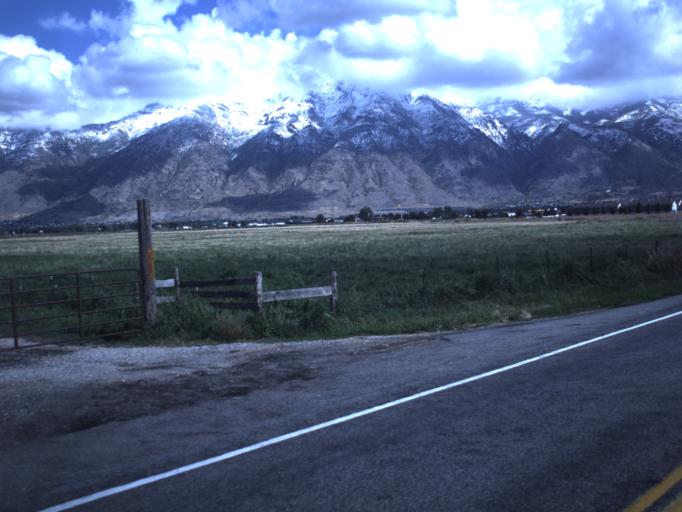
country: US
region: Utah
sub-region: Utah County
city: Spanish Fork
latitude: 40.1586
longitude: -111.6635
